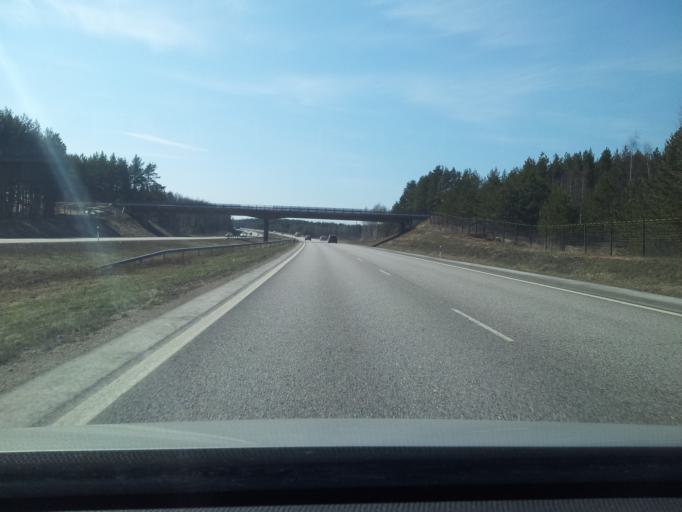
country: FI
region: Kymenlaakso
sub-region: Kotka-Hamina
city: Karhula
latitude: 60.5683
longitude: 27.0499
